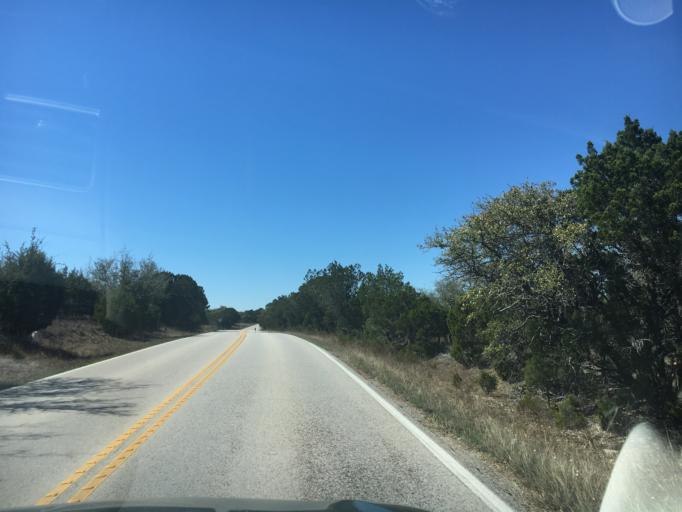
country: US
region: Texas
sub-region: Hays County
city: Dripping Springs
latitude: 30.2910
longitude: -98.0748
